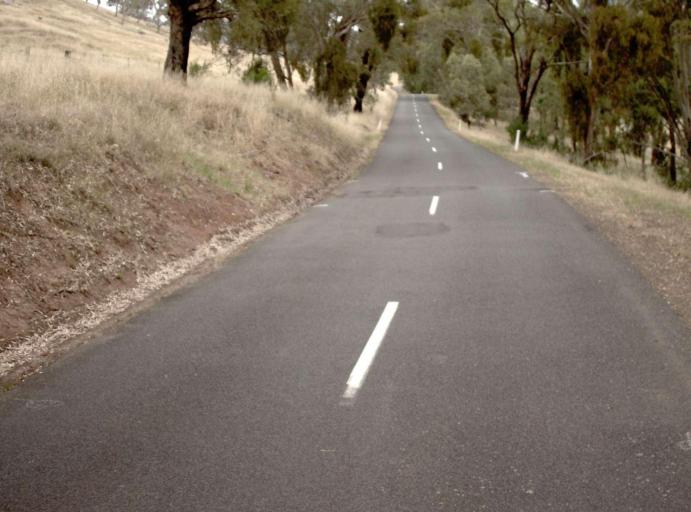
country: AU
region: Victoria
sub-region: Wellington
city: Heyfield
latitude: -37.6802
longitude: 146.6557
